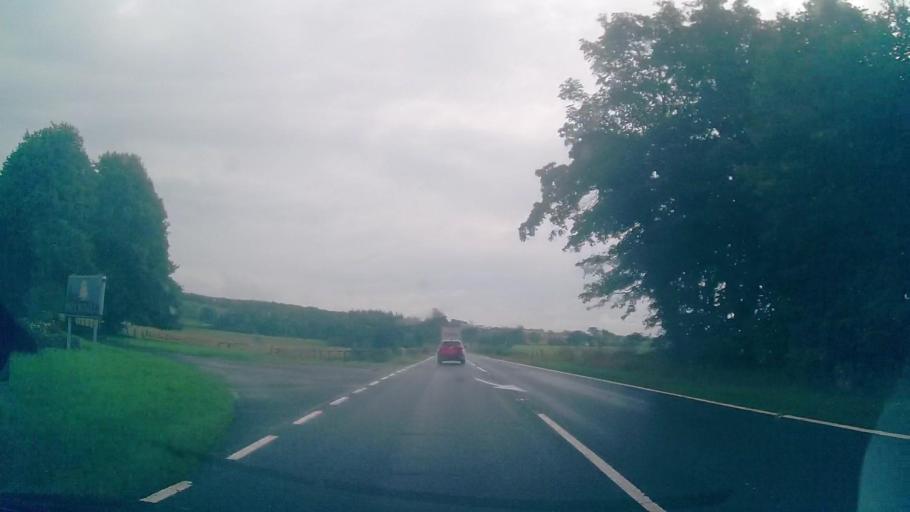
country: GB
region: Scotland
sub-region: Dumfries and Galloway
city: Lochmaben
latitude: 55.0612
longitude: -3.4856
